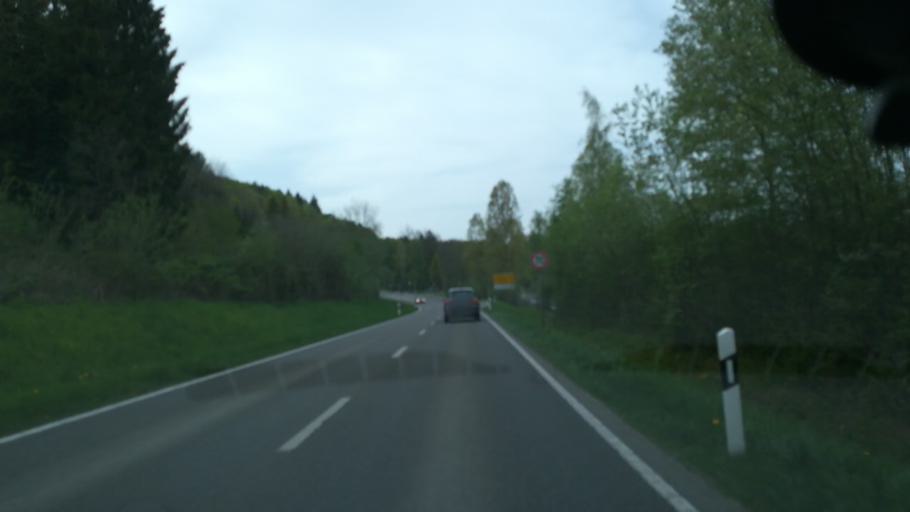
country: DE
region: Baden-Wuerttemberg
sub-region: Freiburg Region
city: Konstanz
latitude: 47.6977
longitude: 9.1832
